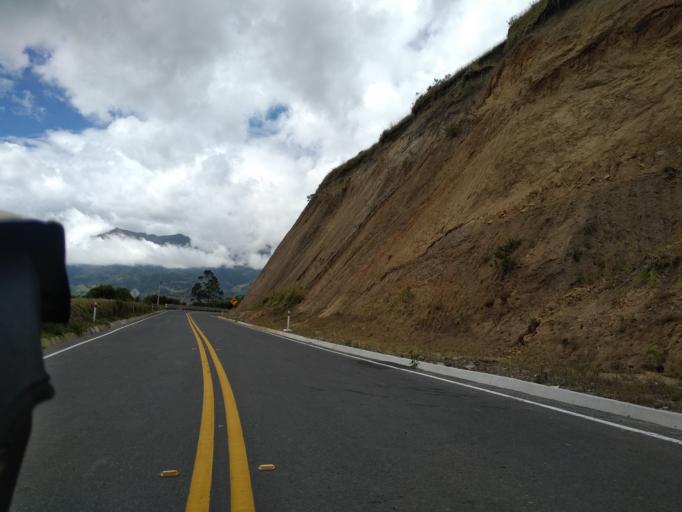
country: EC
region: Cotopaxi
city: Saquisili
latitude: -0.7608
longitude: -78.9092
